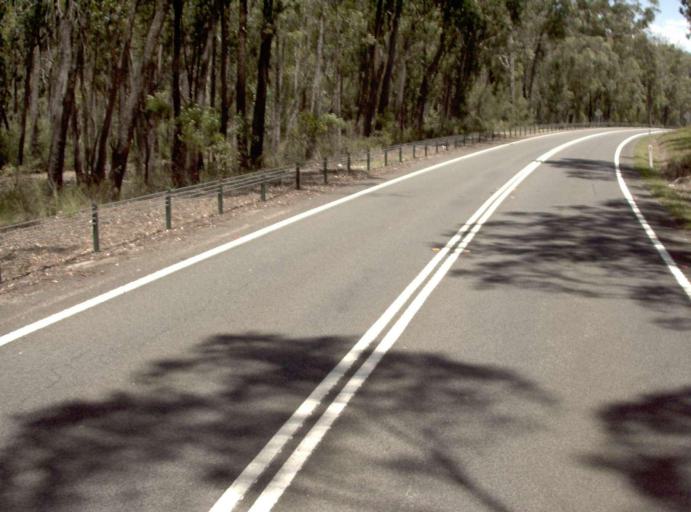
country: AU
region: Victoria
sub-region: East Gippsland
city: Lakes Entrance
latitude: -37.7549
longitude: 148.0664
